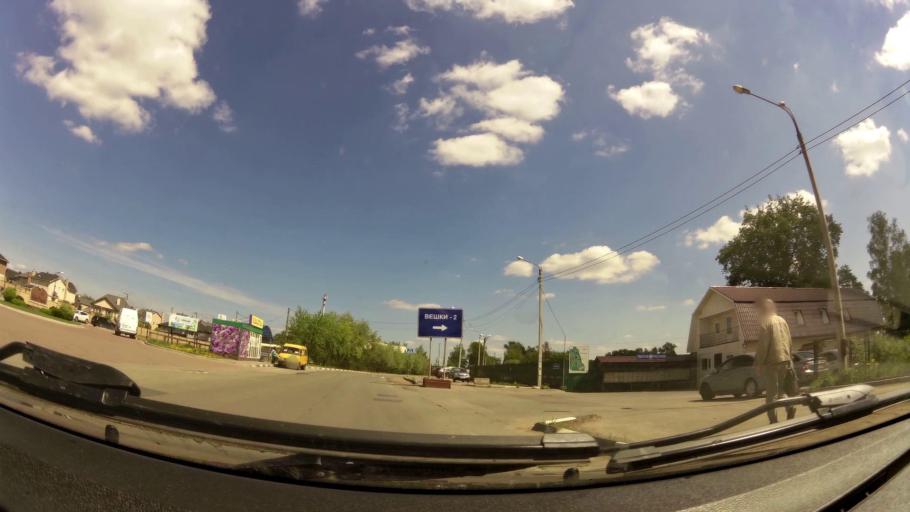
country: RU
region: Moscow
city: Lianozovo
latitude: 55.9252
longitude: 37.6035
